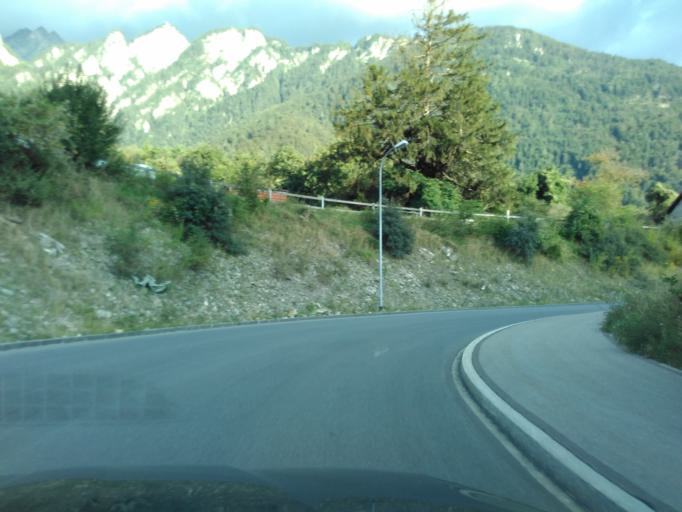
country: CH
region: Grisons
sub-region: Plessur District
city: Chur
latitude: 46.8632
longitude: 9.5445
